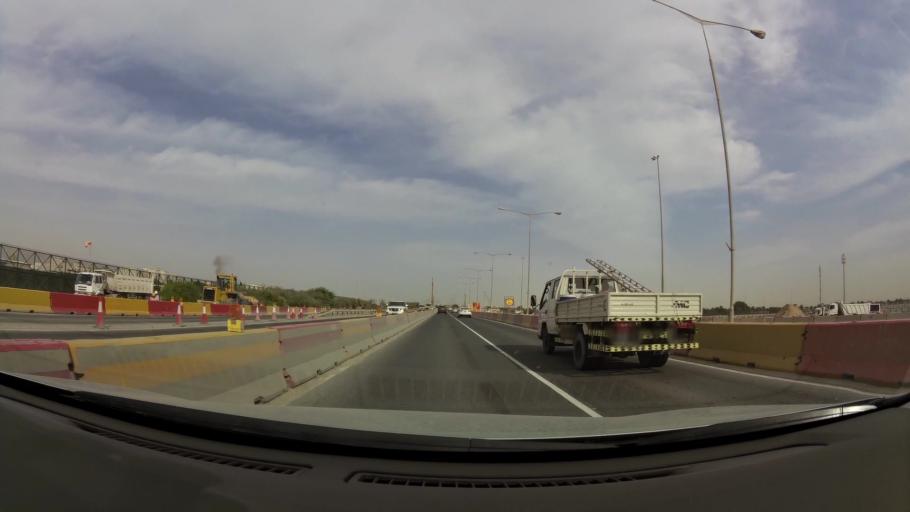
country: QA
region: Baladiyat ar Rayyan
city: Ar Rayyan
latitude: 25.3126
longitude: 51.3846
